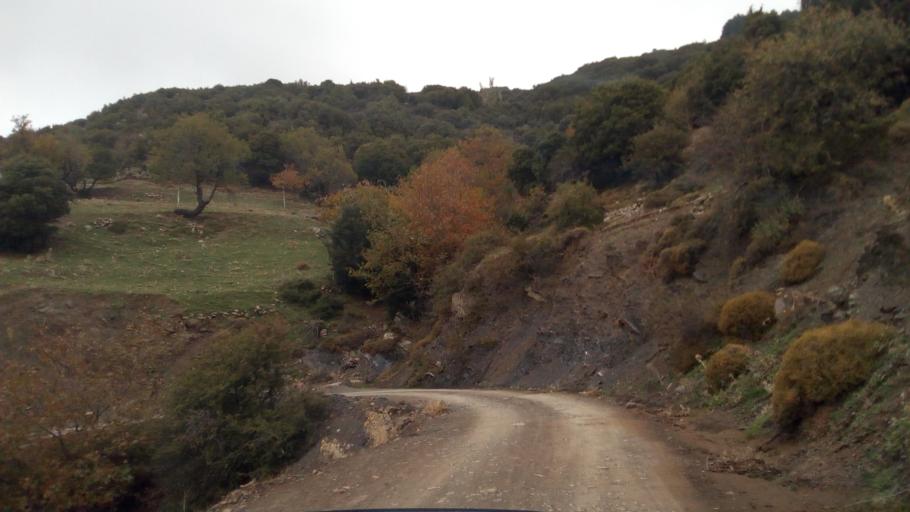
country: GR
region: West Greece
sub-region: Nomos Achaias
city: Selianitika
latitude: 38.4161
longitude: 22.0949
